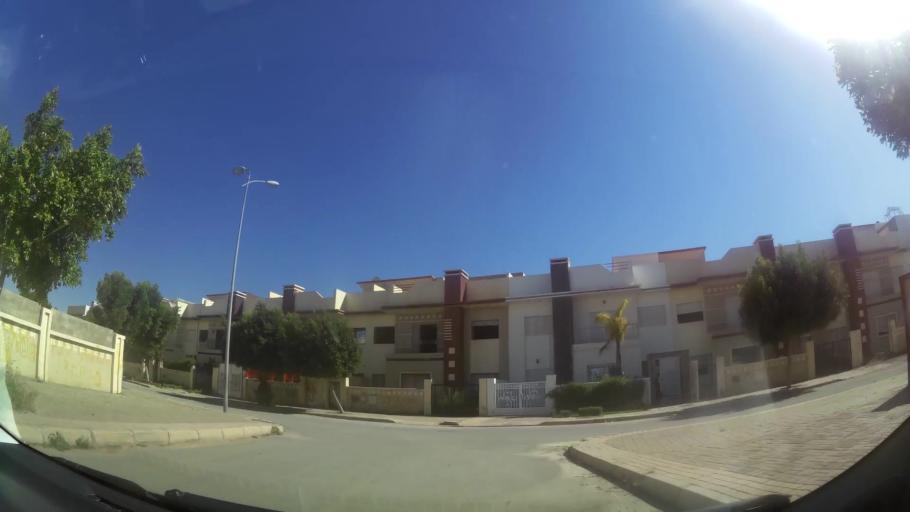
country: MA
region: Oriental
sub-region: Oujda-Angad
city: Oujda
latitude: 34.7238
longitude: -1.9087
